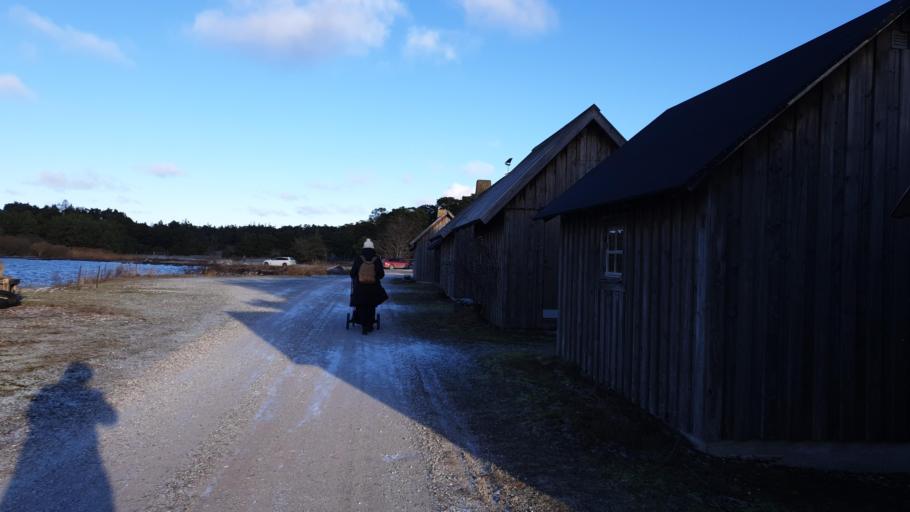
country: SE
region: Gotland
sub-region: Gotland
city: Slite
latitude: 57.3706
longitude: 18.8055
